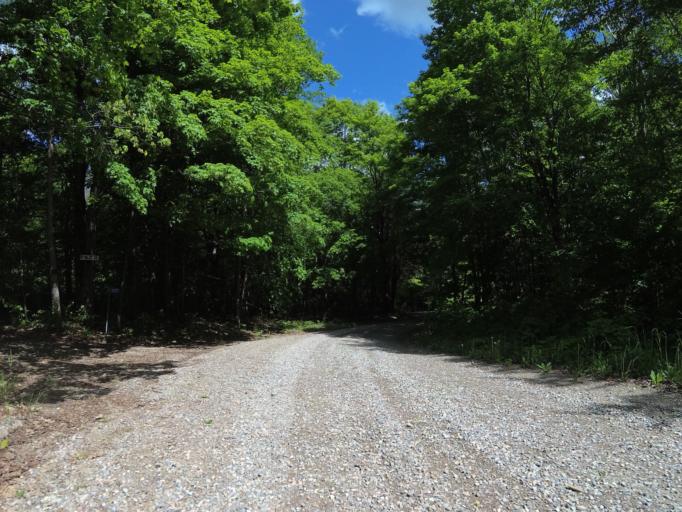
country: CA
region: Ontario
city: Renfrew
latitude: 45.0717
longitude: -76.7602
